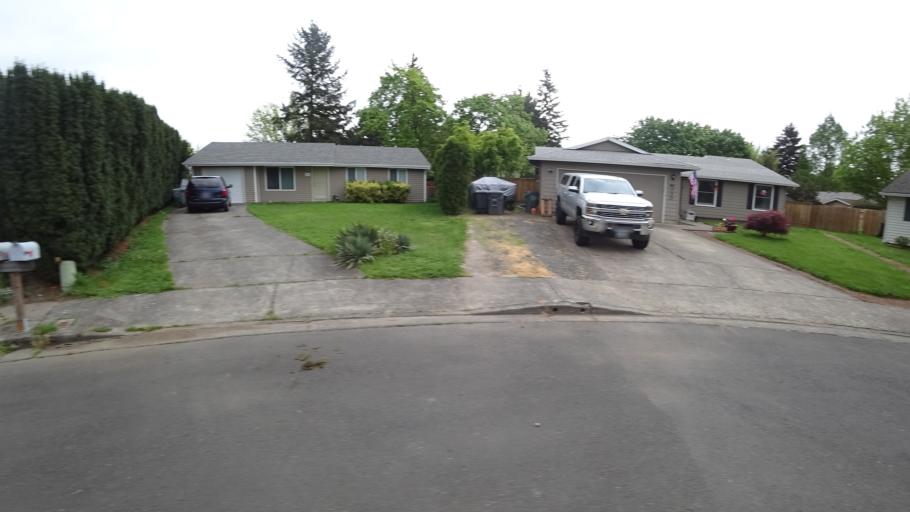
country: US
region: Oregon
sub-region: Washington County
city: Hillsboro
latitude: 45.5394
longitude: -122.9738
